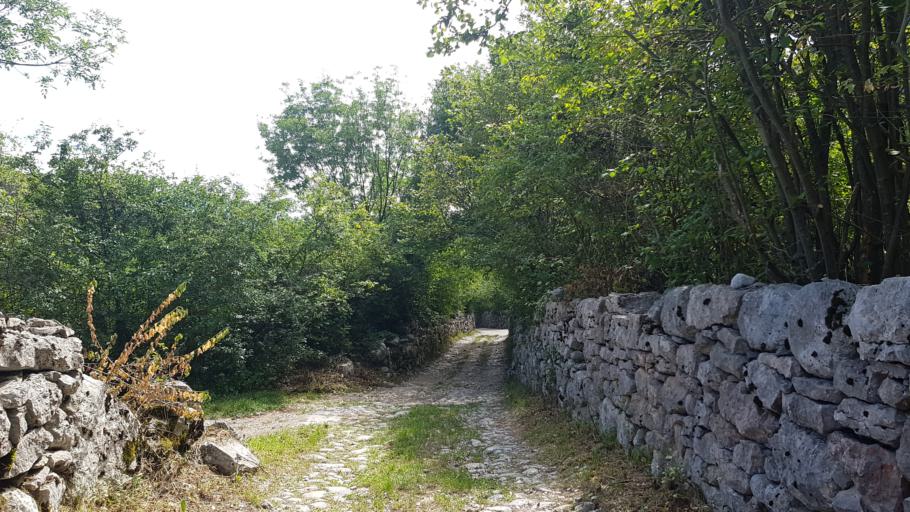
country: IT
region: Trentino-Alto Adige
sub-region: Provincia di Trento
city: Vezzano
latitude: 46.0887
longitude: 10.9940
